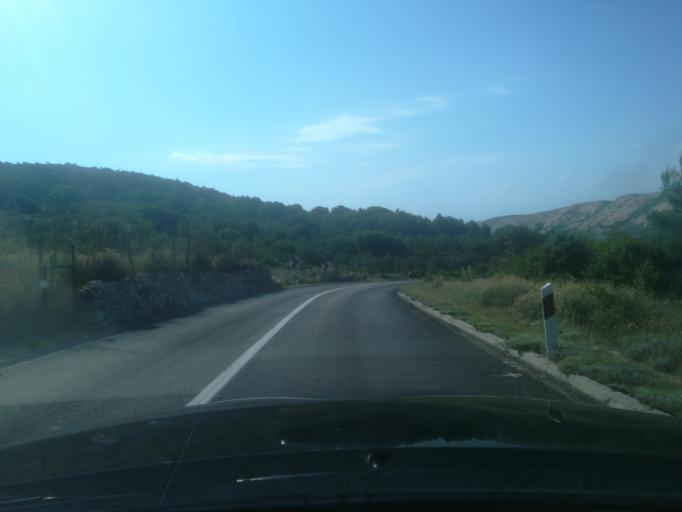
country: HR
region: Primorsko-Goranska
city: Banjol
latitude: 44.7193
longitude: 14.8244
